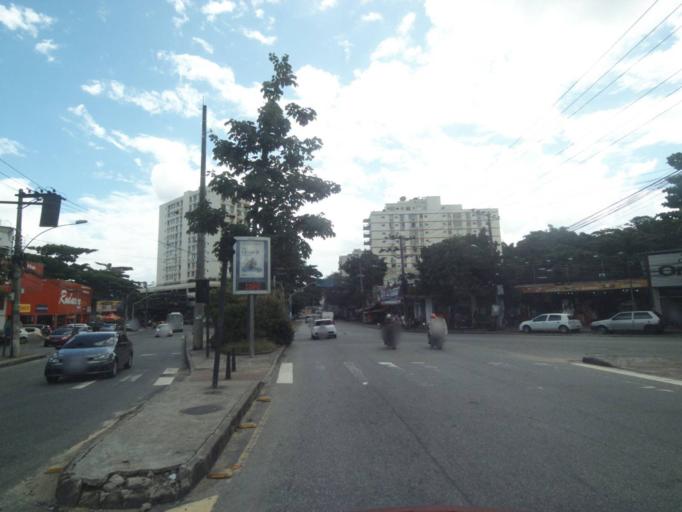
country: BR
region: Rio de Janeiro
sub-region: Sao Joao De Meriti
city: Sao Joao de Meriti
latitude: -22.9291
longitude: -43.3541
